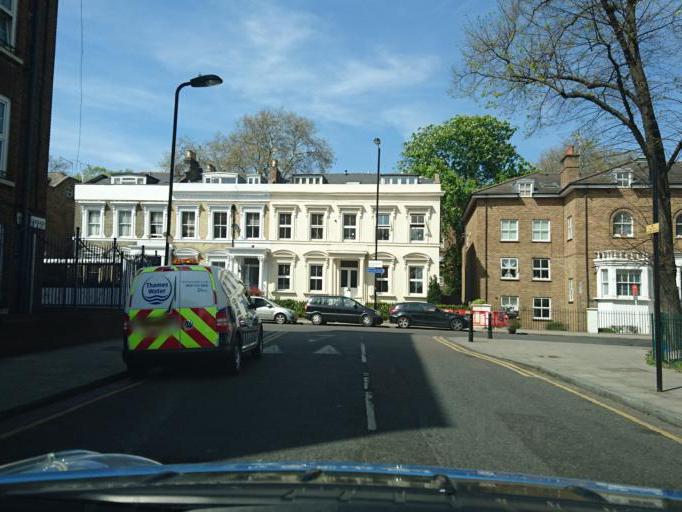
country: GB
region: England
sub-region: Greater London
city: Hackney
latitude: 51.5581
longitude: -0.0577
